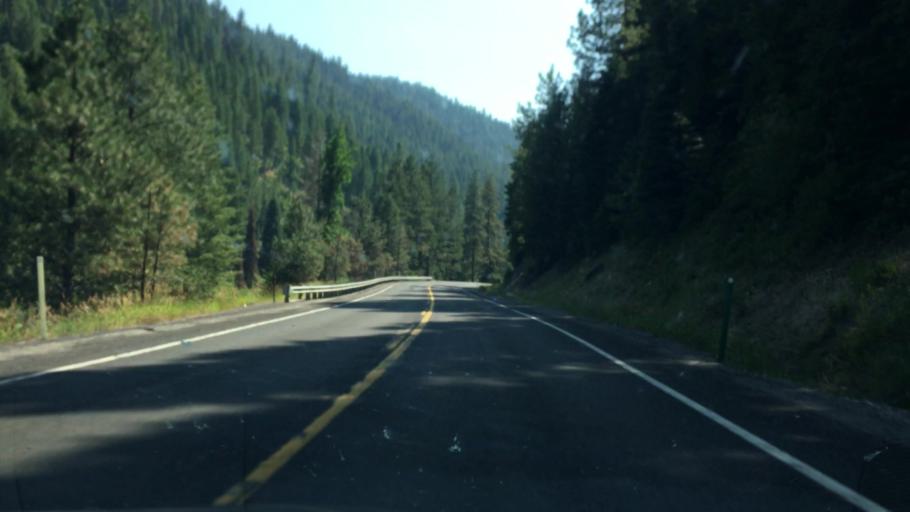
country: US
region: Idaho
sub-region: Valley County
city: Cascade
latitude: 44.2607
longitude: -116.0803
